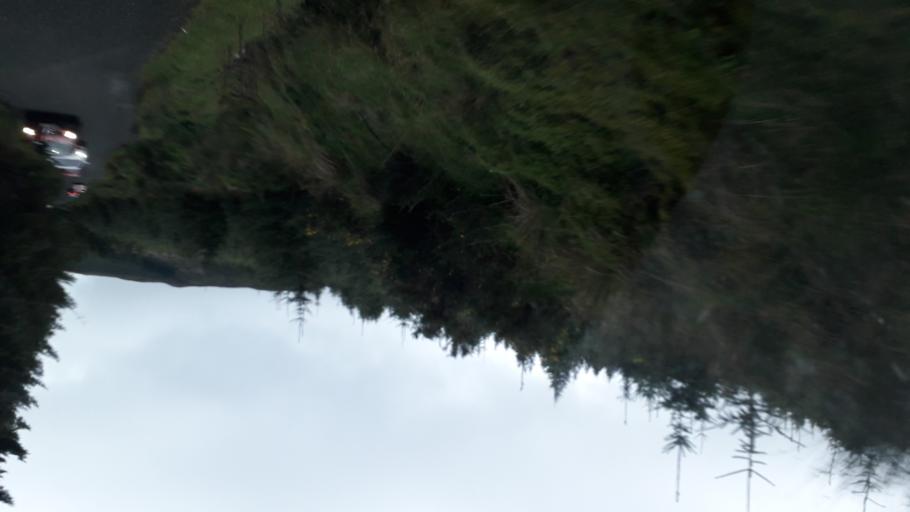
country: IE
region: Leinster
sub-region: Wicklow
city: Enniskerry
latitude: 53.1183
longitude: -6.2688
